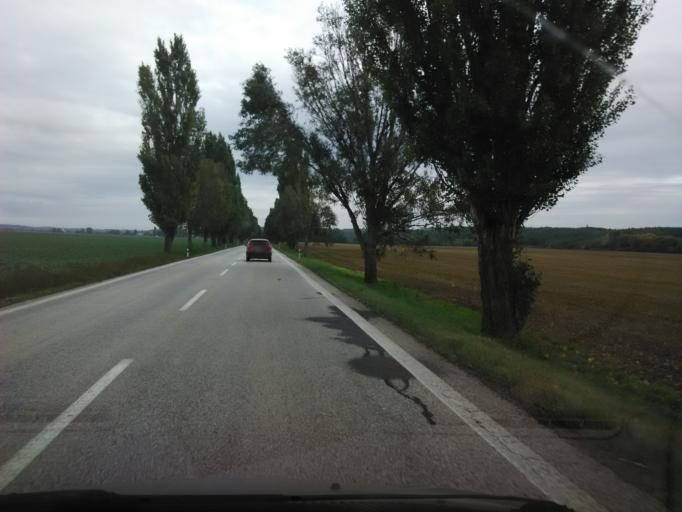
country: SK
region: Nitriansky
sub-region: Okres Nitra
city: Vrable
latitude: 48.2347
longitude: 18.3422
